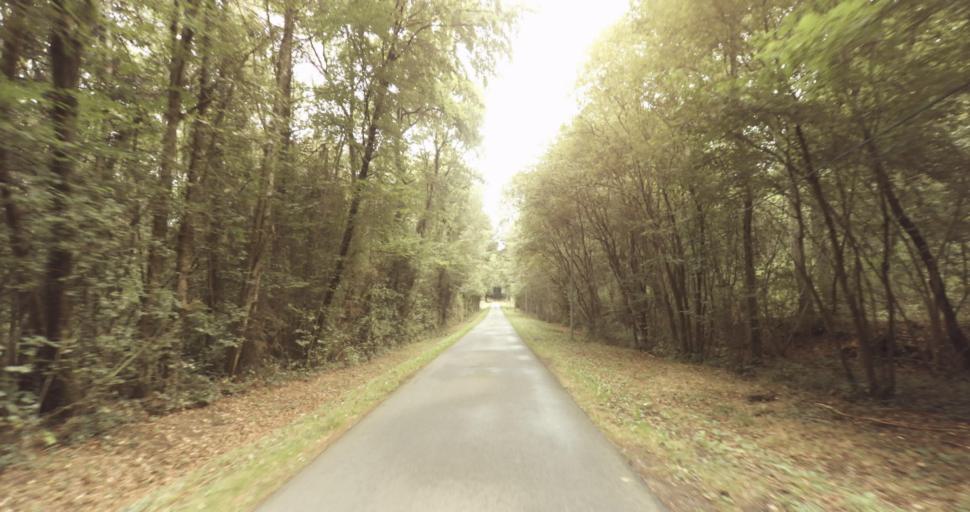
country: FR
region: Lower Normandy
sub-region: Departement de l'Orne
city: Gace
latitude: 48.6837
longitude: 0.2621
